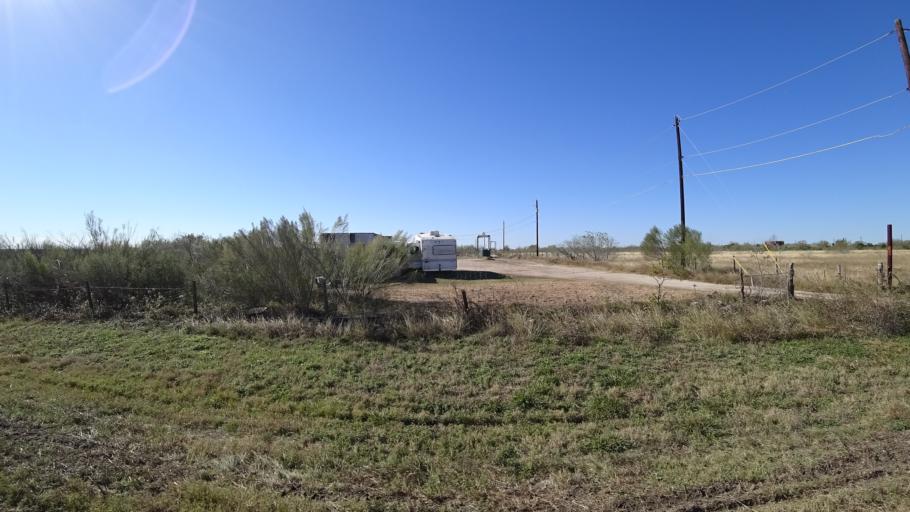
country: US
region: Texas
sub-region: Travis County
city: Garfield
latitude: 30.1218
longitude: -97.6289
